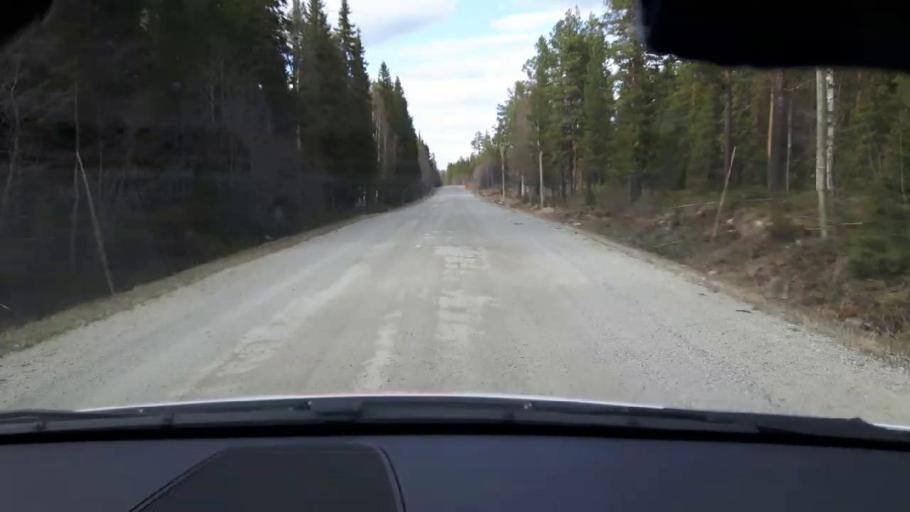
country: SE
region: Jaemtland
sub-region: Bergs Kommun
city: Hoverberg
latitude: 62.6702
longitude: 14.7461
